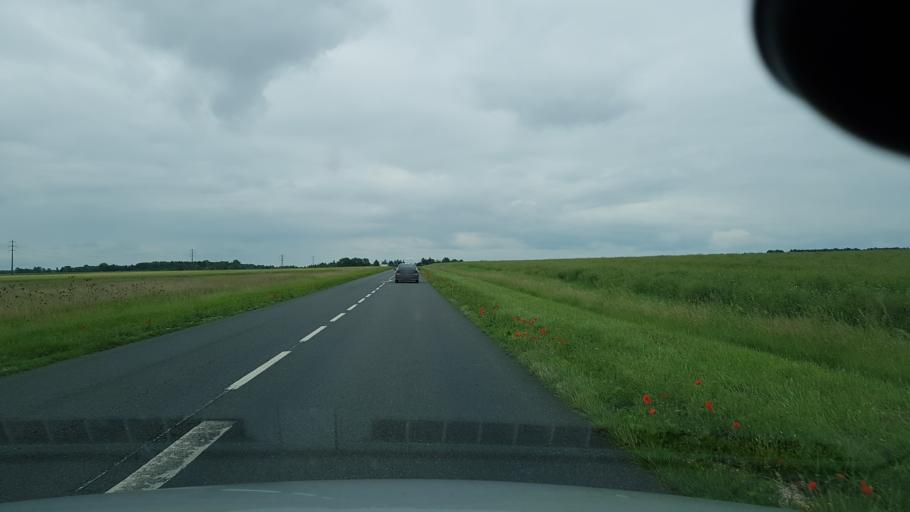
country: FR
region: Centre
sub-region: Departement du Loir-et-Cher
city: Chatillon-sur-Cher
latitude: 47.2993
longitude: 1.5149
